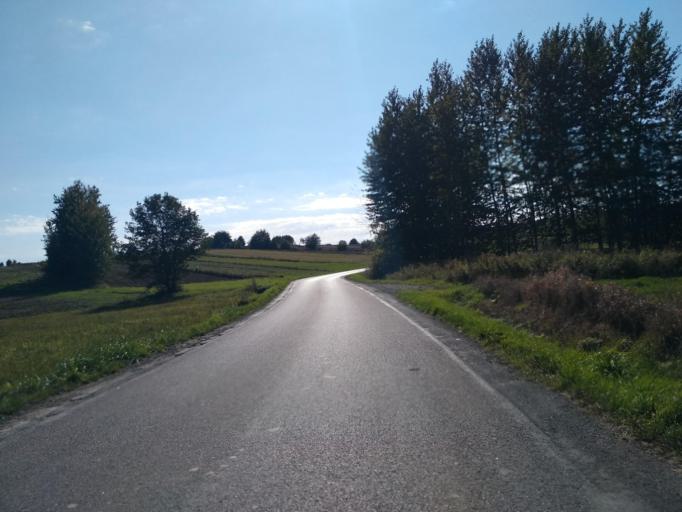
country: PL
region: Subcarpathian Voivodeship
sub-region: Powiat debicki
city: Slotowa
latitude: 49.9561
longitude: 21.2936
